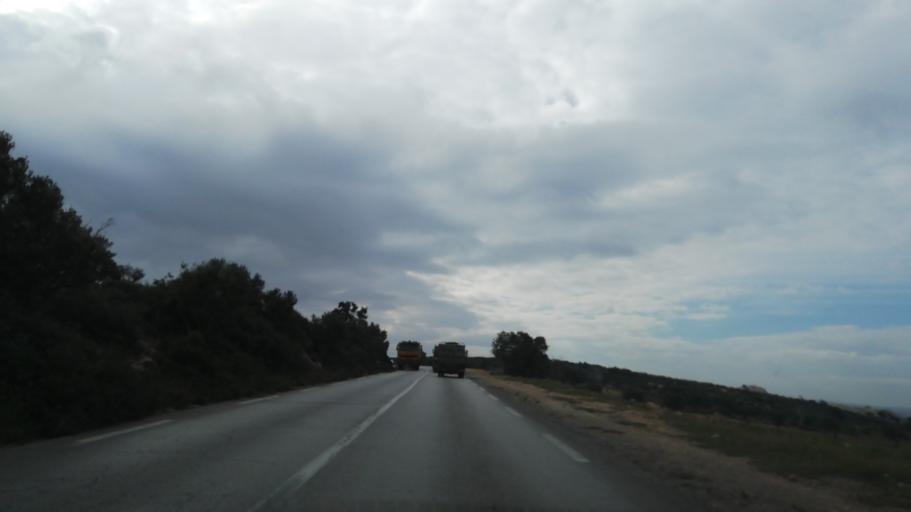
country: DZ
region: Oran
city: Ain el Bya
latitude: 35.7213
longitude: -0.3573
